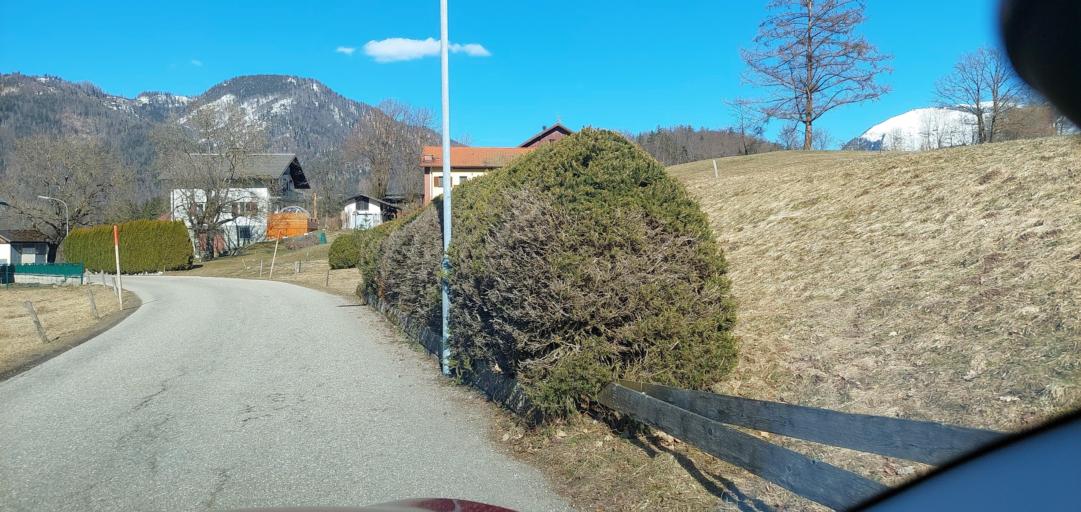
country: AT
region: Upper Austria
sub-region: Politischer Bezirk Gmunden
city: Bad Ischl
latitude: 47.7121
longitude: 13.5999
